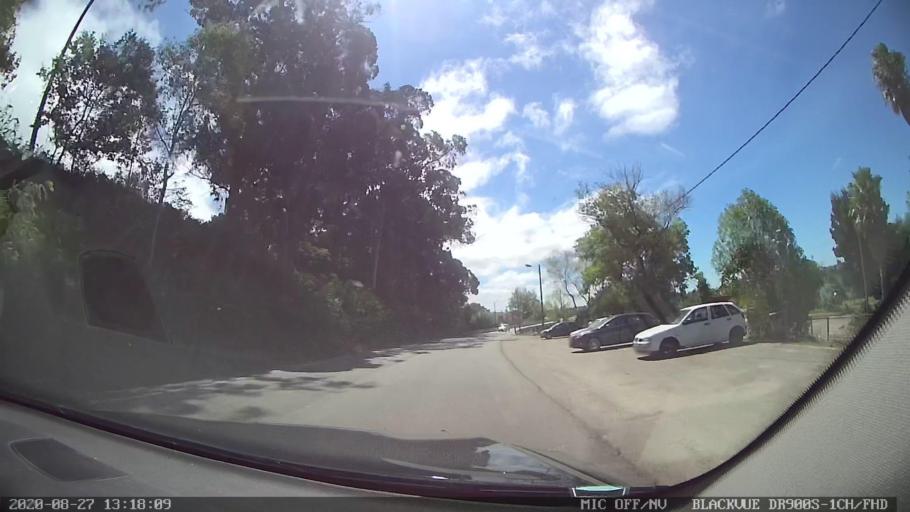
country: PT
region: Aveiro
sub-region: Vagos
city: Vagos
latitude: 40.5759
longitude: -8.6791
